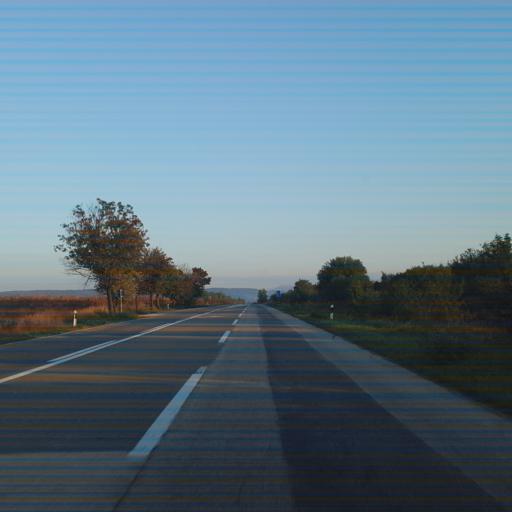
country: RS
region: Central Serbia
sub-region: Zajecarski Okrug
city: Zajecar
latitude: 44.0370
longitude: 22.3397
